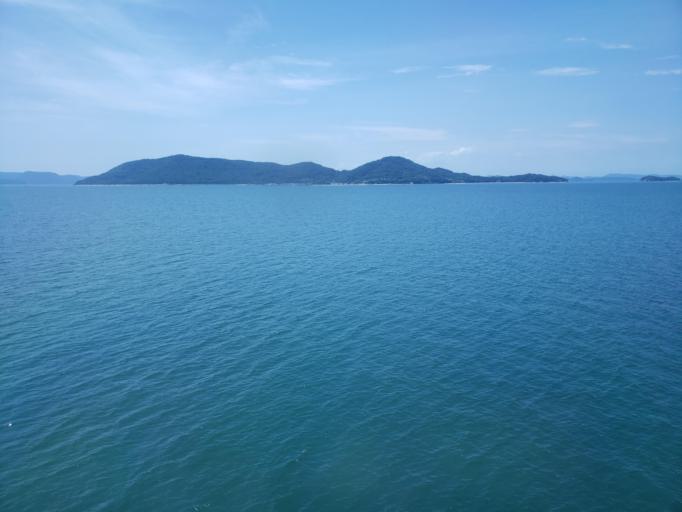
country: JP
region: Kagawa
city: Takamatsu-shi
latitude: 34.3796
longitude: 134.0859
